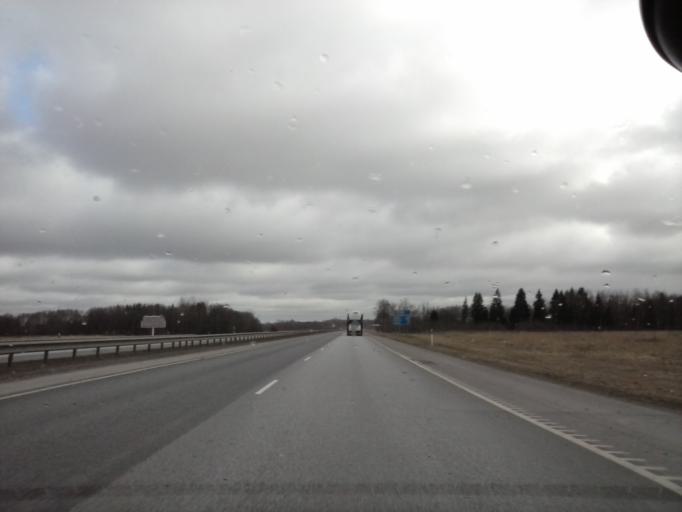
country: EE
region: Harju
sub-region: Rae vald
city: Jueri
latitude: 59.3443
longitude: 24.8959
